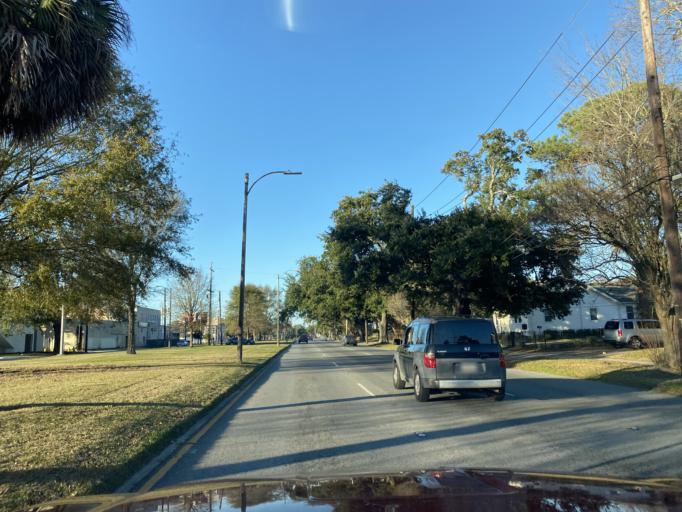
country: US
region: Louisiana
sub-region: Orleans Parish
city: New Orleans
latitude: 29.9971
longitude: -90.0590
